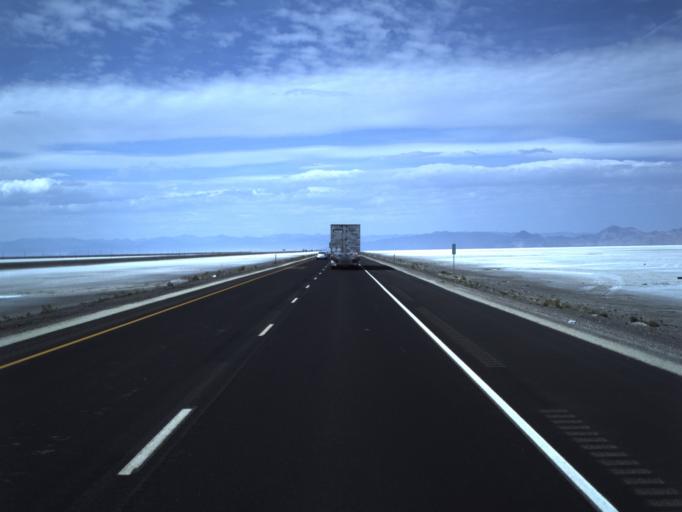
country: US
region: Utah
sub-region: Tooele County
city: Wendover
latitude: 40.7347
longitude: -113.6258
